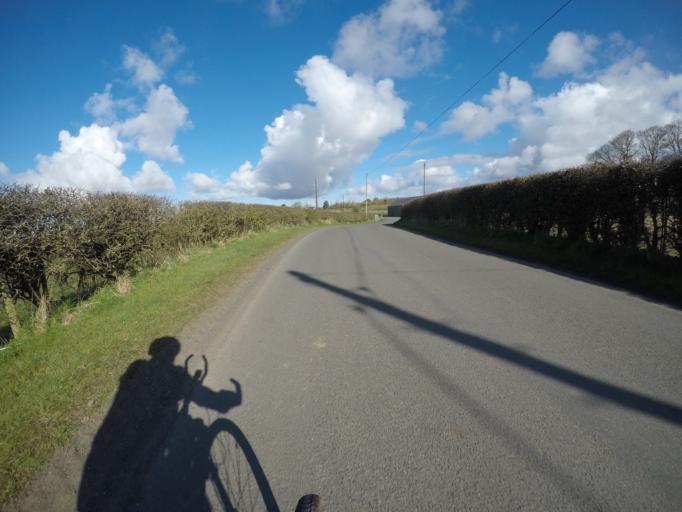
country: GB
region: Scotland
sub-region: North Ayrshire
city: Irvine
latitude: 55.6549
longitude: -4.6529
